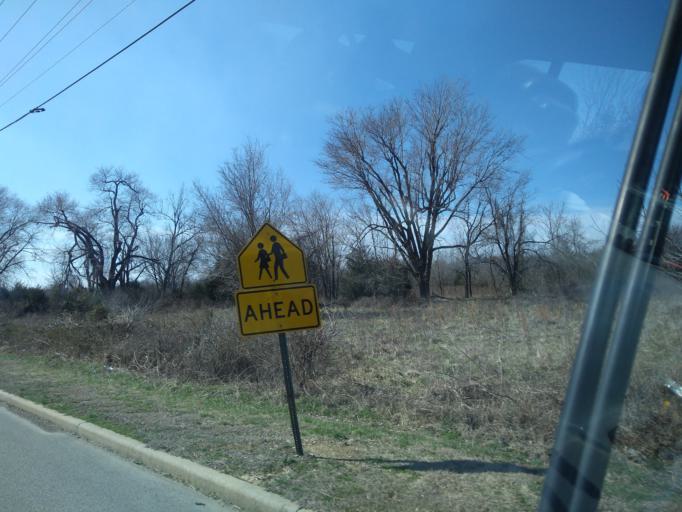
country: US
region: Arkansas
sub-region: Washington County
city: Farmington
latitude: 36.0560
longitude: -94.2359
